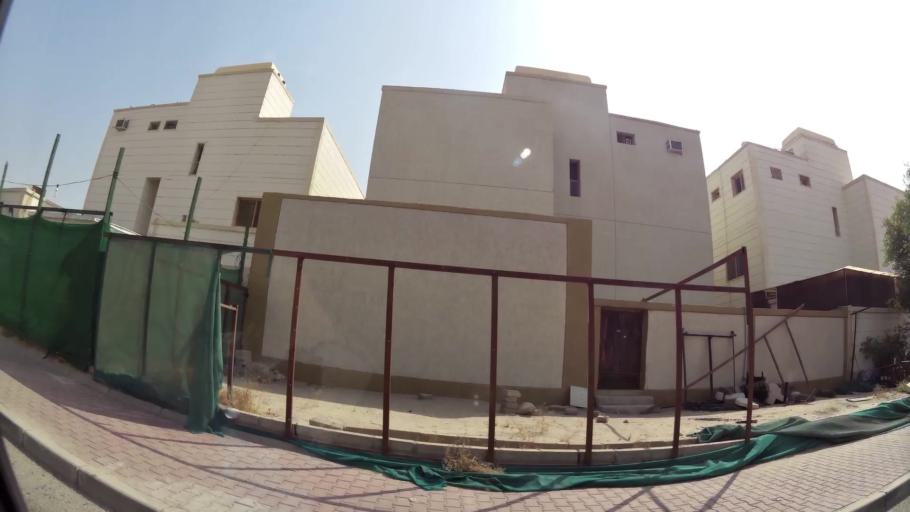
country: KW
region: Muhafazat al Jahra'
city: Al Jahra'
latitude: 29.3243
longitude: 47.7244
